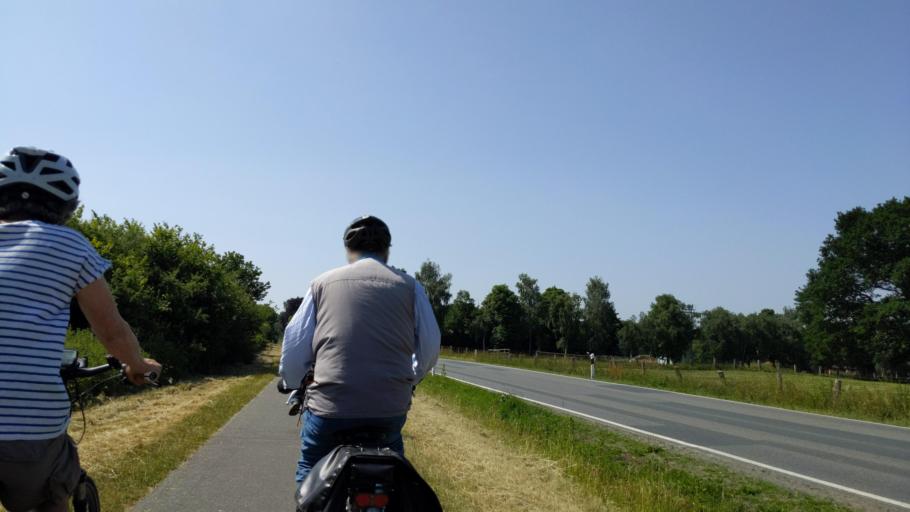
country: DE
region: Schleswig-Holstein
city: Berkenthin
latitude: 53.7498
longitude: 10.6567
